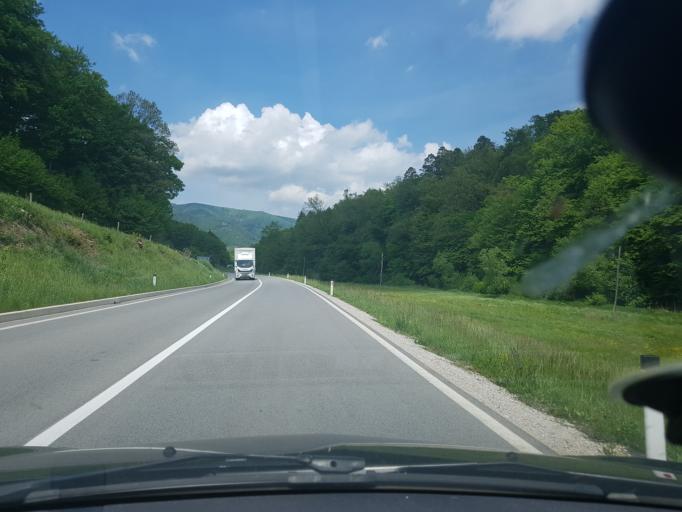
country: SI
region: Rogatec
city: Rogatec
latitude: 46.2294
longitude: 15.6750
